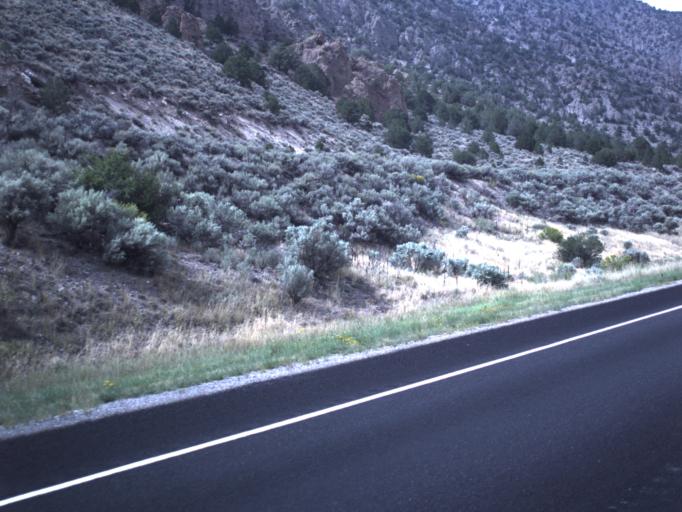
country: US
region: Utah
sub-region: Piute County
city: Junction
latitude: 38.0790
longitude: -112.3399
